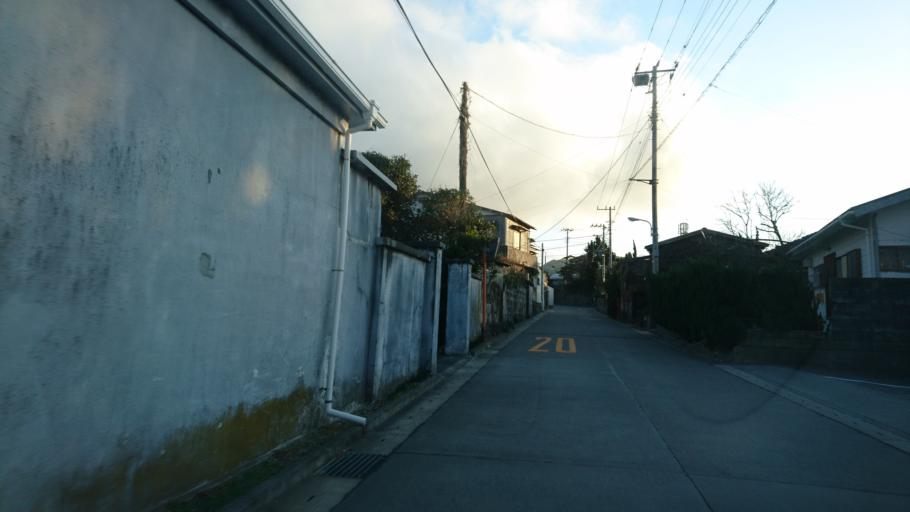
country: JP
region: Shizuoka
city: Shimoda
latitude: 34.3761
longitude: 139.2574
